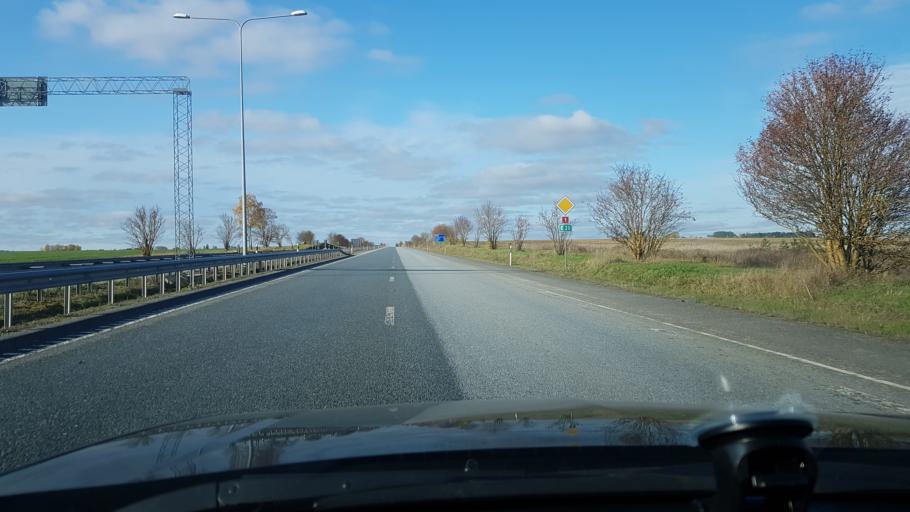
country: EE
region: Laeaene-Virumaa
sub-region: Haljala vald
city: Haljala
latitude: 59.4248
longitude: 26.2624
